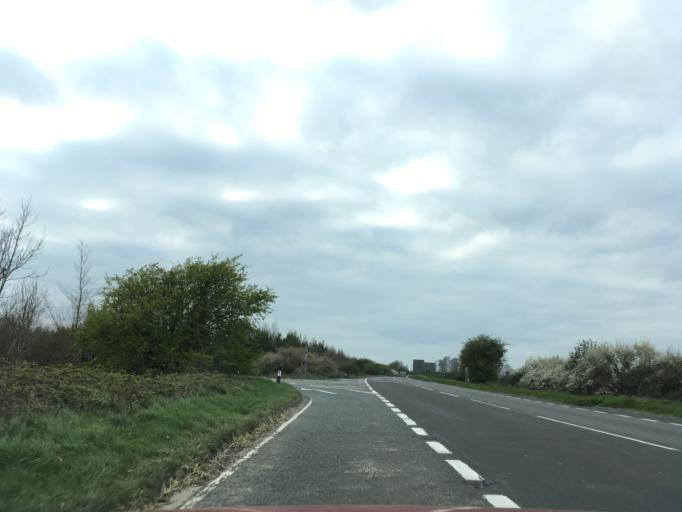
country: GB
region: England
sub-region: Oxfordshire
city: Burford
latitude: 51.8076
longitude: -1.6616
